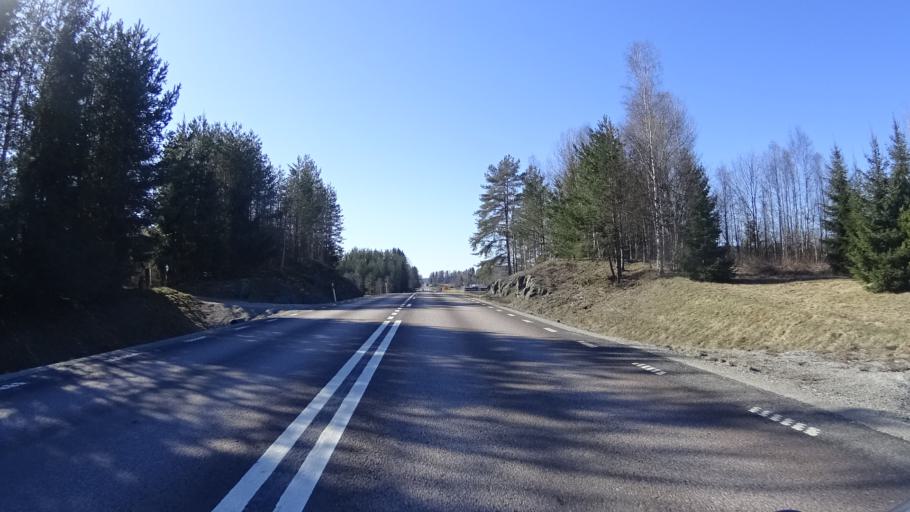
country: SE
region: Vaermland
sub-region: Arvika Kommun
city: Arvika
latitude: 59.6652
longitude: 12.8688
